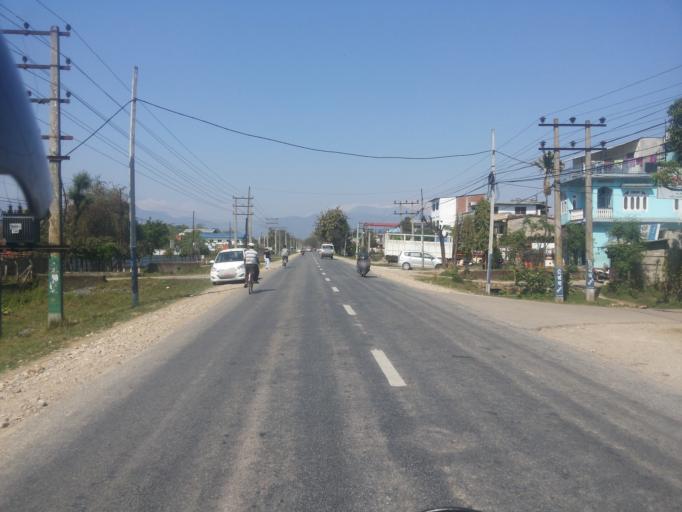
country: NP
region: Central Region
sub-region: Narayani Zone
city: Bharatpur
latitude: 27.6752
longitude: 84.4388
